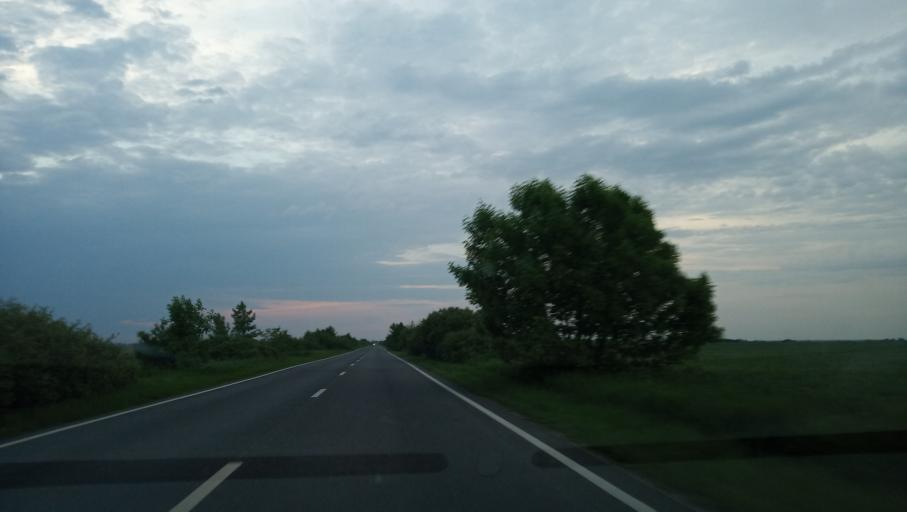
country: RO
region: Timis
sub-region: Comuna Jebel
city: Jebel
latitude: 45.5370
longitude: 21.2276
